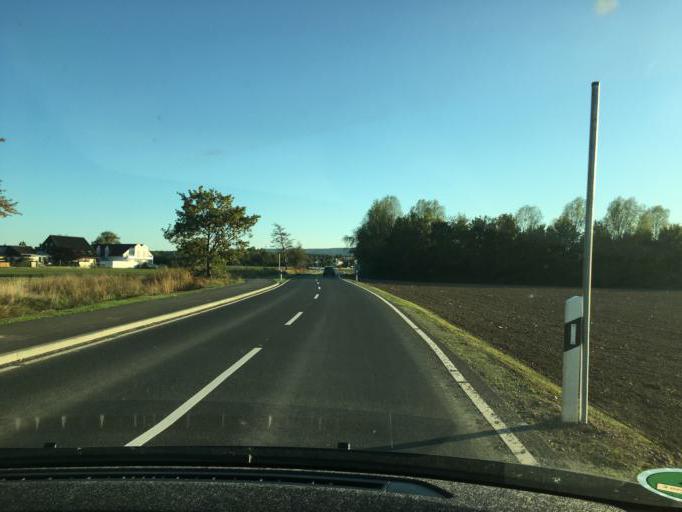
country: DE
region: North Rhine-Westphalia
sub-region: Regierungsbezirk Koln
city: Langerwehe
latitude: 50.8084
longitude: 6.3958
